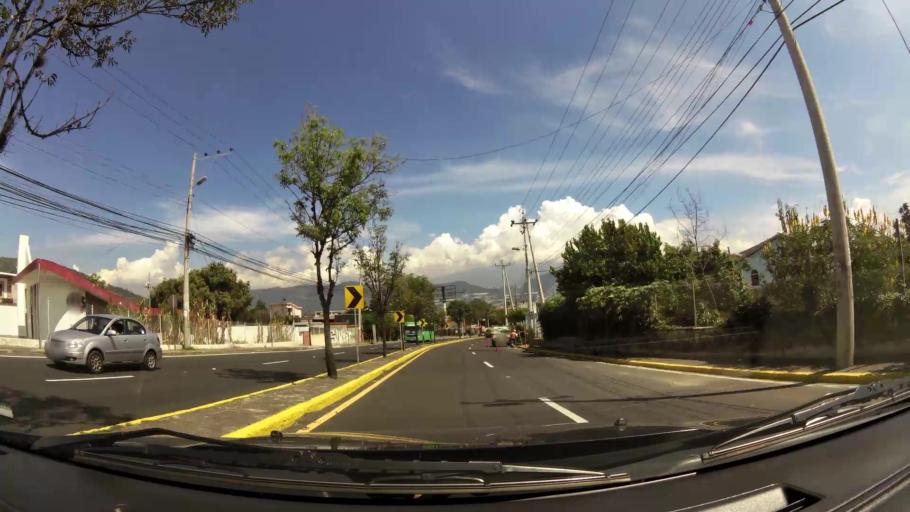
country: EC
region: Pichincha
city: Quito
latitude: -0.2173
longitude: -78.4006
